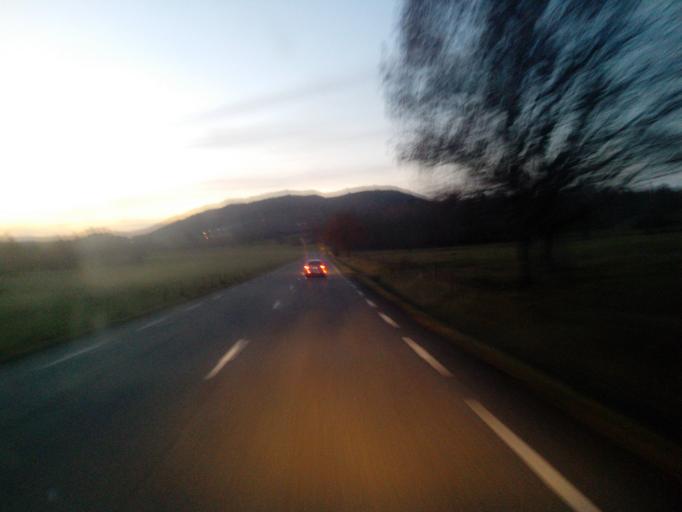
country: FR
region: Midi-Pyrenees
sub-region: Departement de l'Ariege
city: Foix
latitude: 43.0088
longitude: 1.5214
